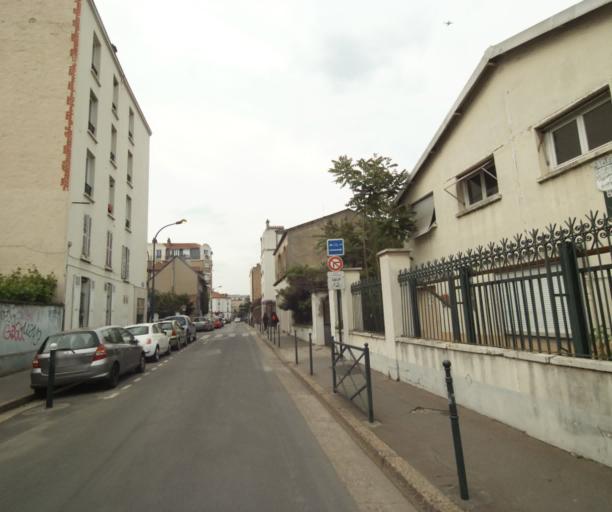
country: FR
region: Ile-de-France
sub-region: Departement des Hauts-de-Seine
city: Asnieres-sur-Seine
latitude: 48.9201
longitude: 2.2846
